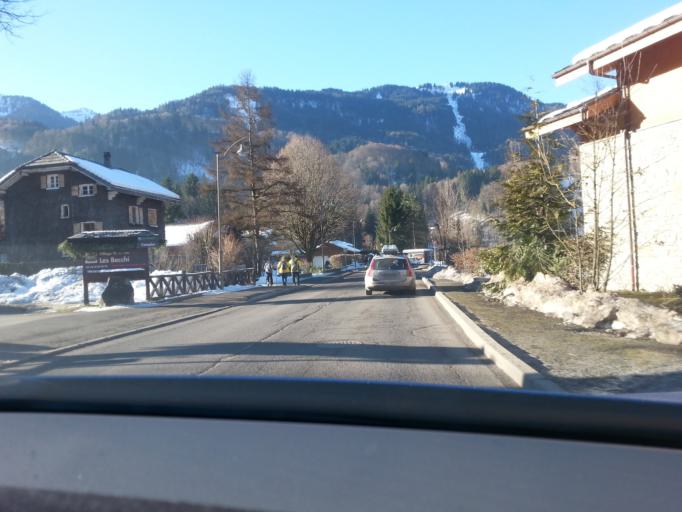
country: FR
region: Rhone-Alpes
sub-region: Departement de la Haute-Savoie
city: Samoens
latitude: 46.0788
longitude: 6.7255
